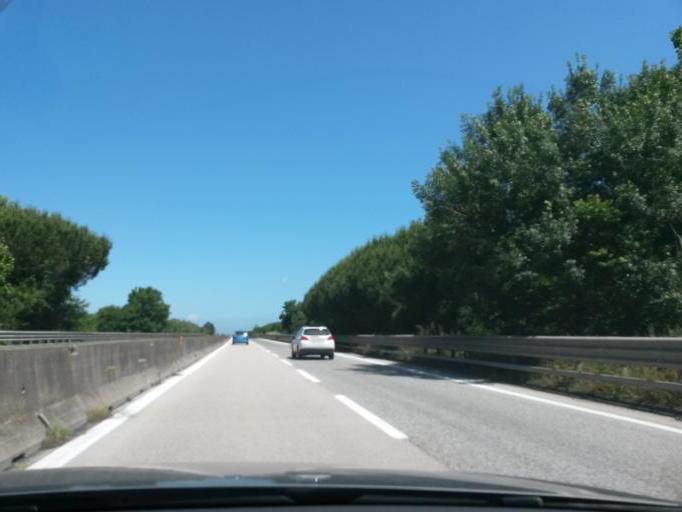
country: IT
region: Tuscany
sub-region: Provincia di Livorno
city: Donoratico
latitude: 43.2098
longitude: 10.5629
